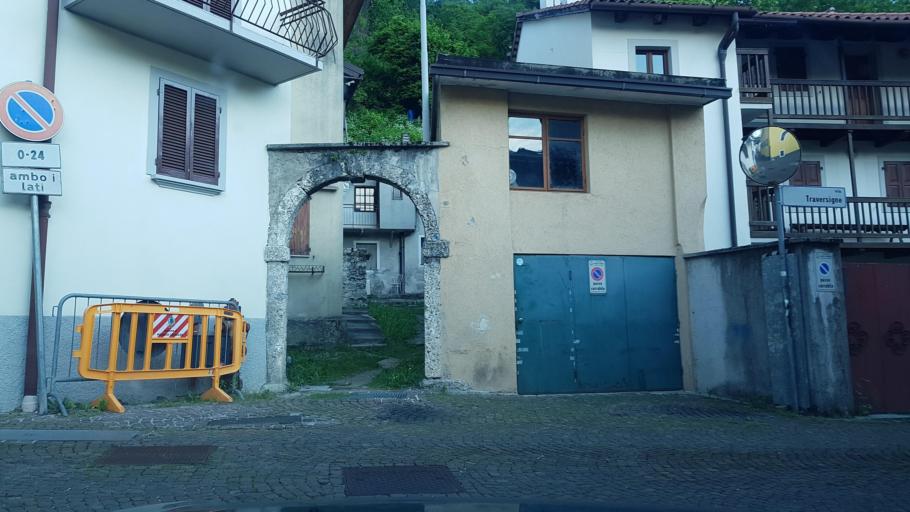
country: IT
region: Friuli Venezia Giulia
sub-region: Provincia di Udine
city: Moggio di Sotto
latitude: 46.4111
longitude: 13.1956
